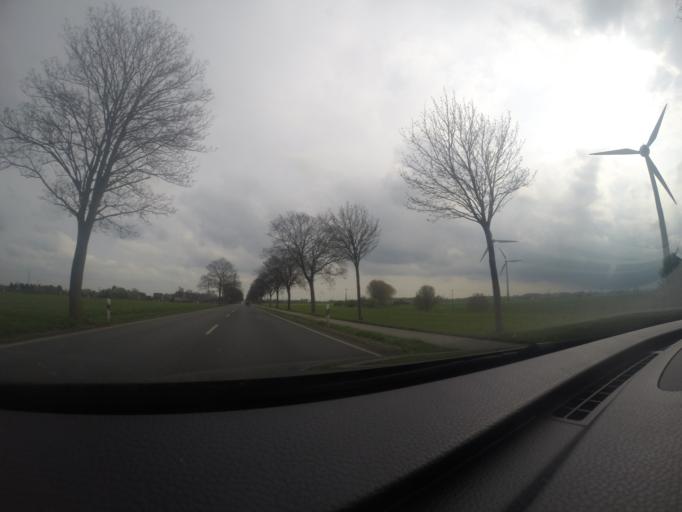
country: DE
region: North Rhine-Westphalia
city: Rheinberg
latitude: 51.5728
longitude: 6.5660
